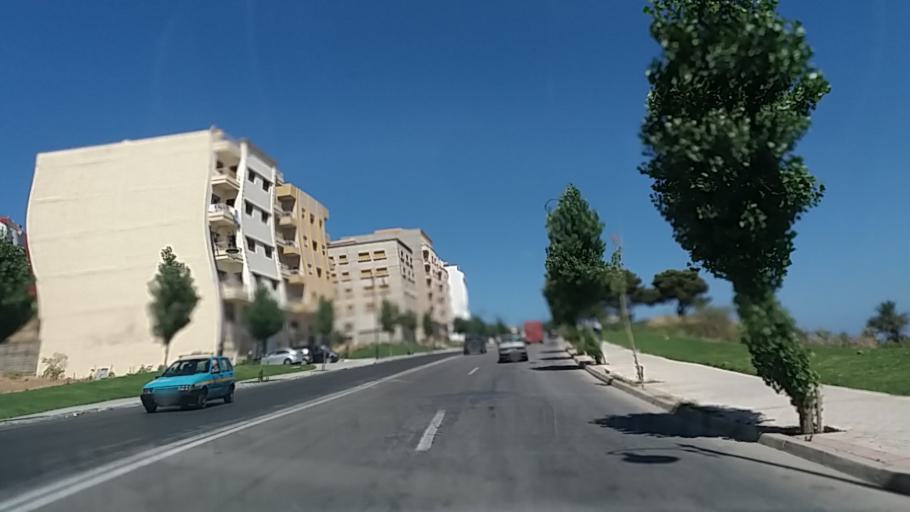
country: MA
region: Tanger-Tetouan
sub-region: Tanger-Assilah
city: Tangier
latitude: 35.7694
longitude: -5.7630
